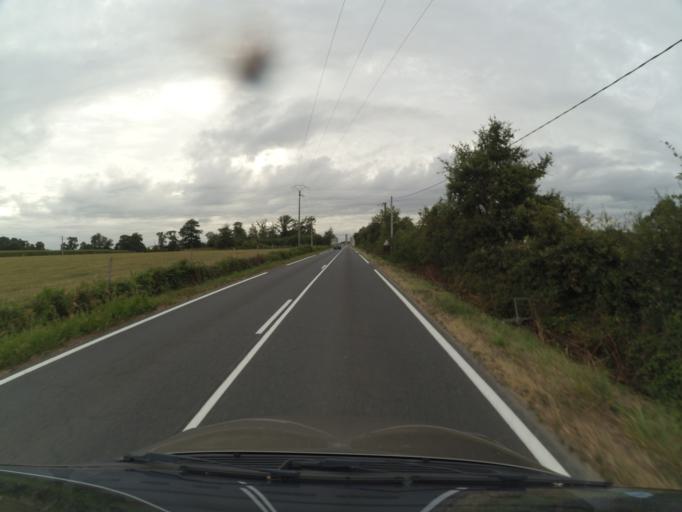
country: FR
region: Pays de la Loire
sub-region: Departement de Maine-et-Loire
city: Torfou
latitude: 47.0313
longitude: -1.0894
